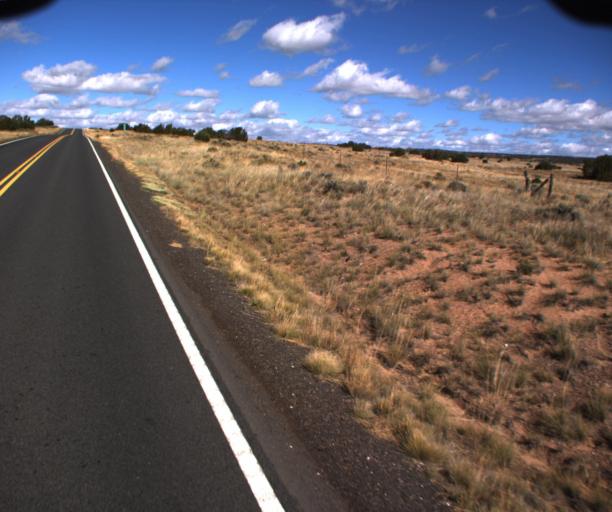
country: US
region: Arizona
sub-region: Apache County
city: Houck
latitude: 35.0186
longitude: -109.2400
